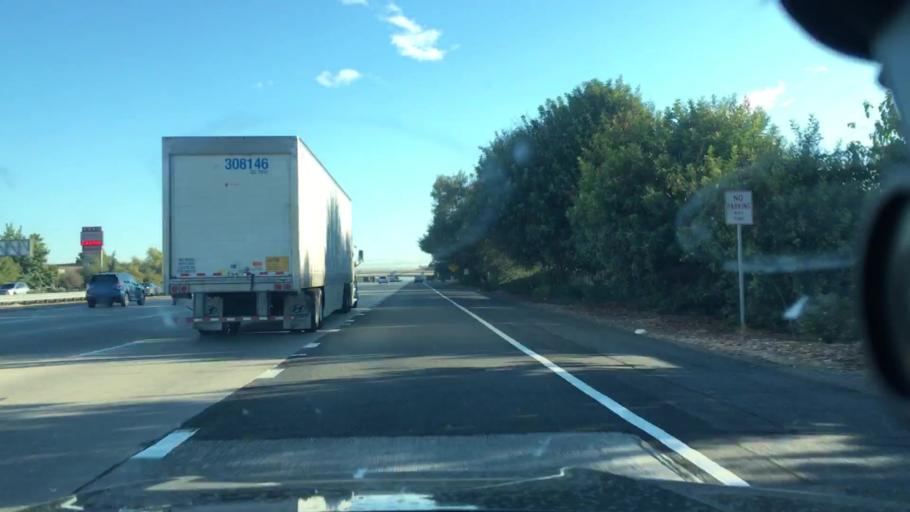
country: US
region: California
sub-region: Sacramento County
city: Antelope
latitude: 38.7033
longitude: -121.3135
